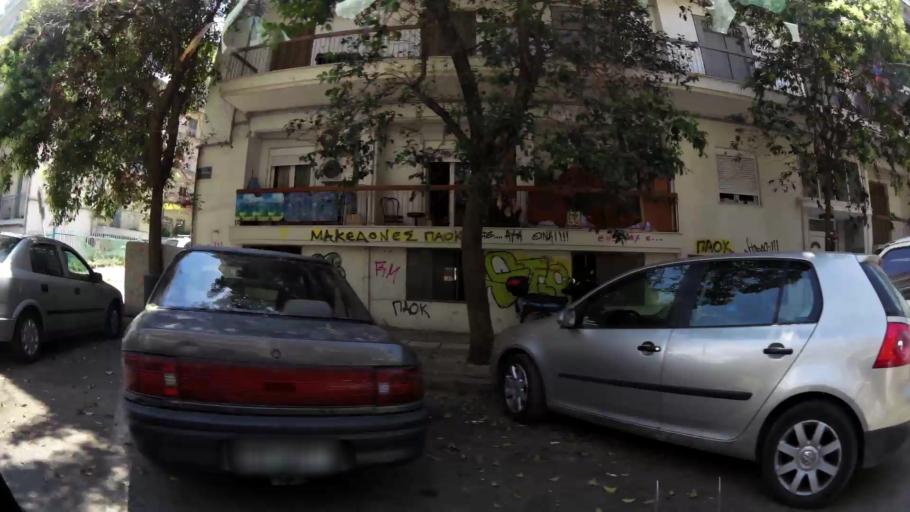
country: GR
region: Central Macedonia
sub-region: Nomos Thessalonikis
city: Triandria
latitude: 40.6088
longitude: 22.9598
